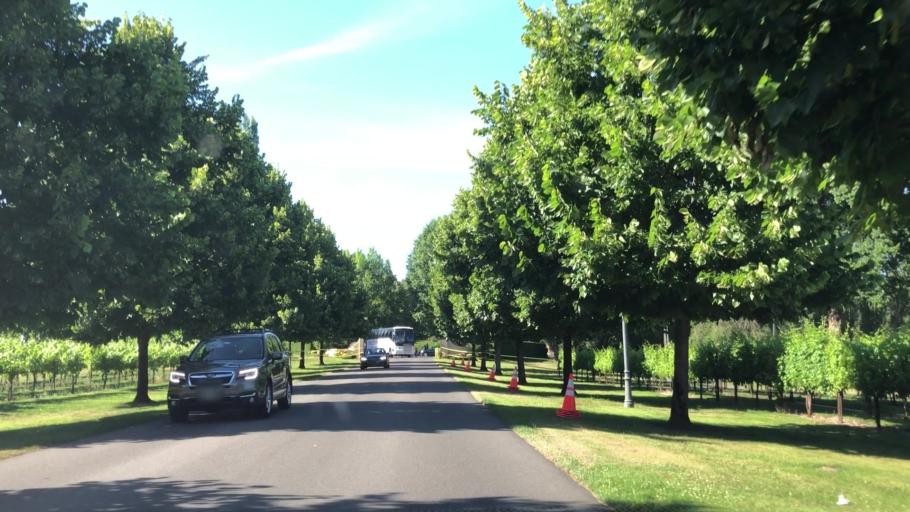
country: US
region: Washington
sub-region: King County
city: Woodinville
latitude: 47.7317
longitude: -122.1510
